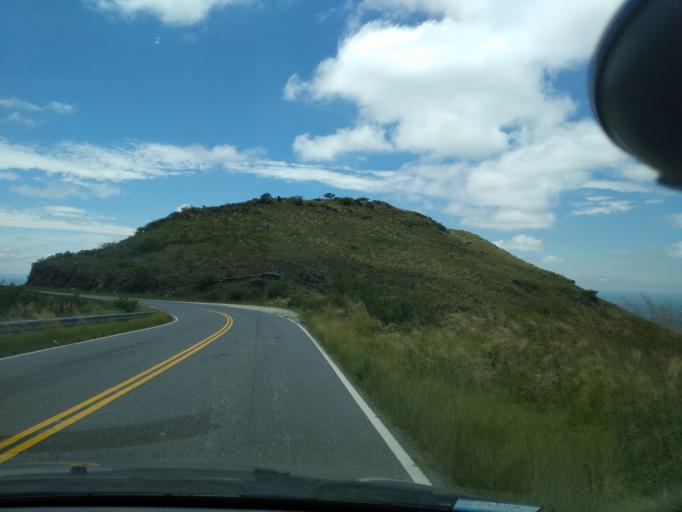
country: AR
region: Cordoba
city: Cuesta Blanca
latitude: -31.5955
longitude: -64.5393
